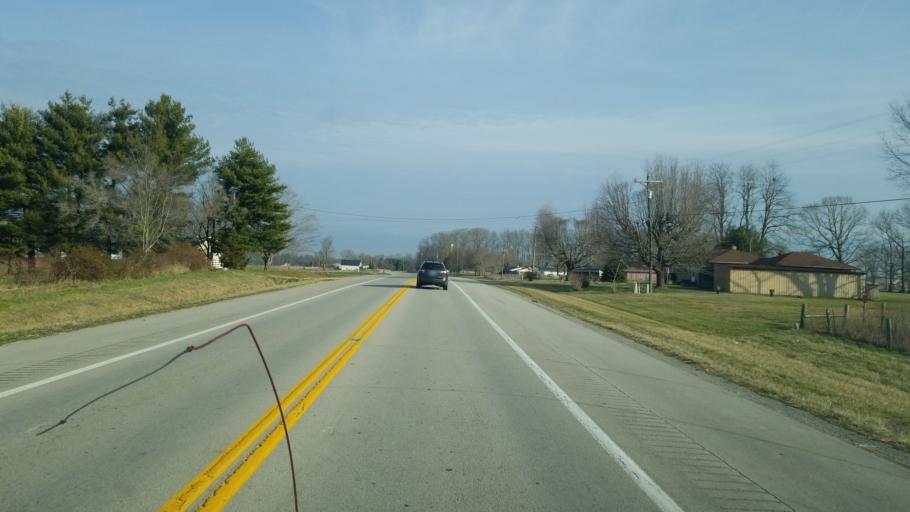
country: US
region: Kentucky
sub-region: Russell County
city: Russell Springs
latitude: 37.1392
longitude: -85.0326
